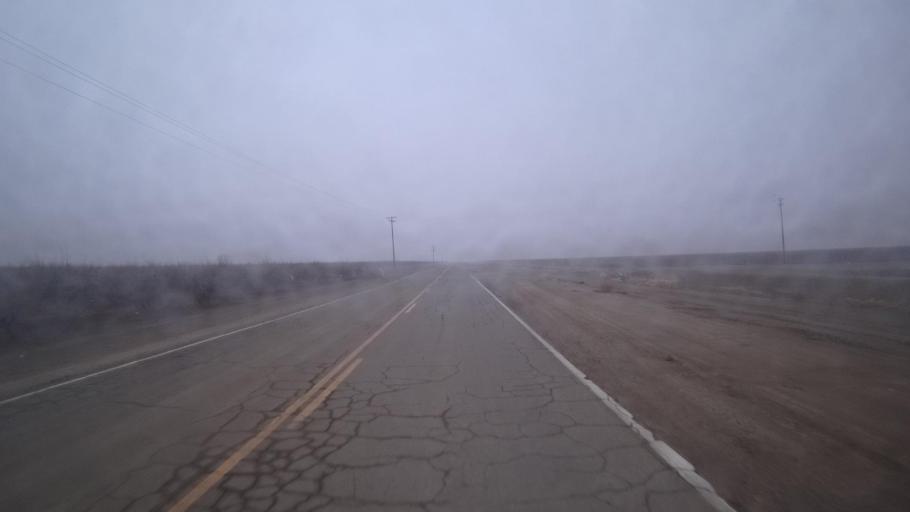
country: US
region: California
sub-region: Kern County
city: Lost Hills
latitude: 35.5132
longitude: -119.6149
